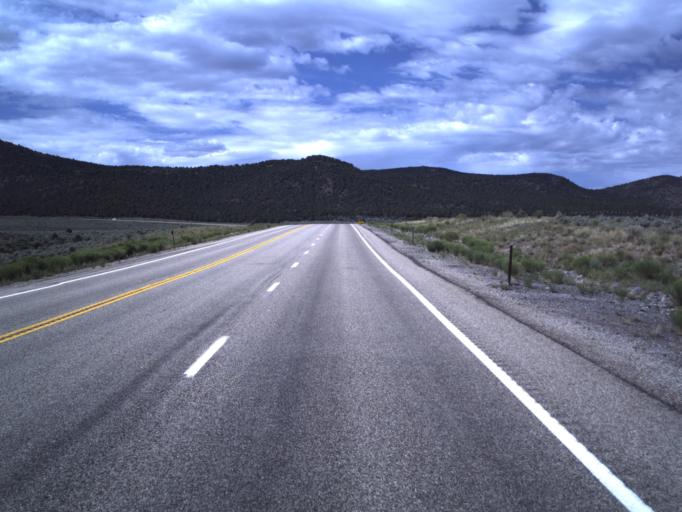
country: US
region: Utah
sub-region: Garfield County
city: Panguitch
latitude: 38.0152
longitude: -112.5093
